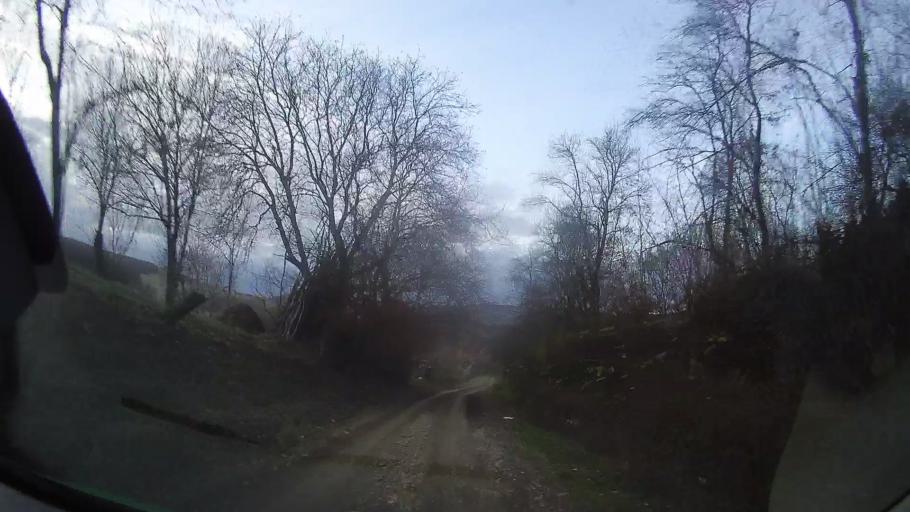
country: RO
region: Cluj
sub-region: Comuna Palatca
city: Palatca
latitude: 46.8620
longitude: 24.0239
